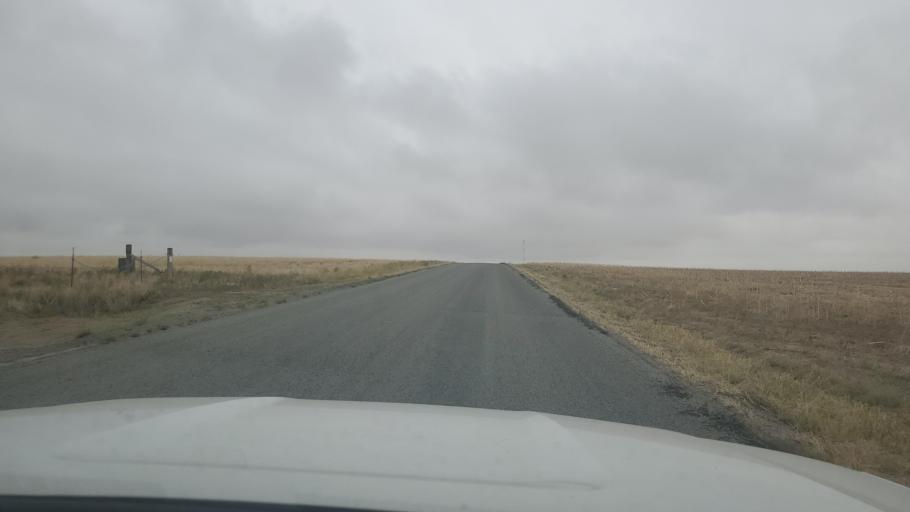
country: US
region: Colorado
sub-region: Weld County
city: Lochbuie
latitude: 39.9357
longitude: -104.6030
